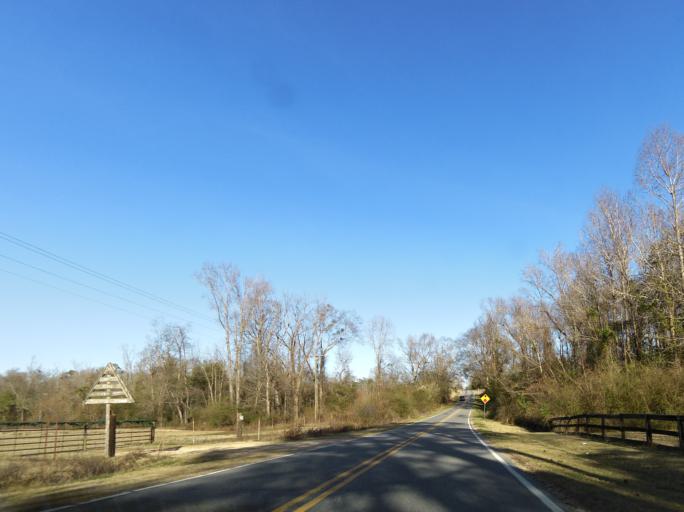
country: US
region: Georgia
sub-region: Bibb County
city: West Point
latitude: 32.7758
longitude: -83.8242
